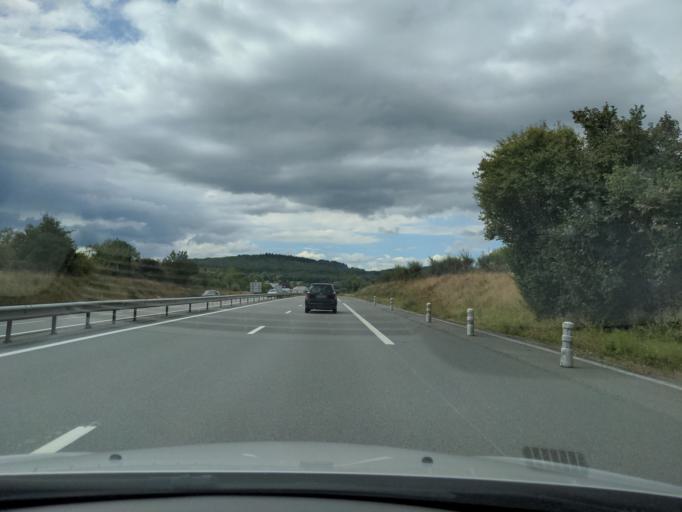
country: FR
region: Limousin
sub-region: Departement de la Creuse
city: Saint-Sulpice-le-Gueretois
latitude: 46.1854
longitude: 1.8376
